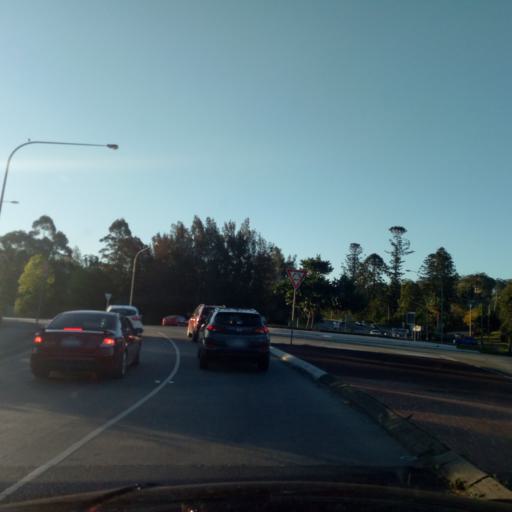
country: AU
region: New South Wales
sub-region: Gosford Shire
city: Narara
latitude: -33.4042
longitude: 151.3505
